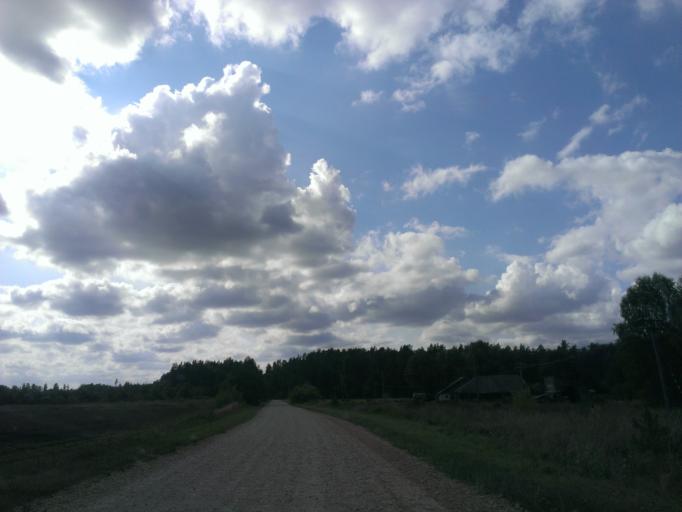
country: LV
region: Incukalns
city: Vangazi
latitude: 57.1202
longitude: 24.5647
